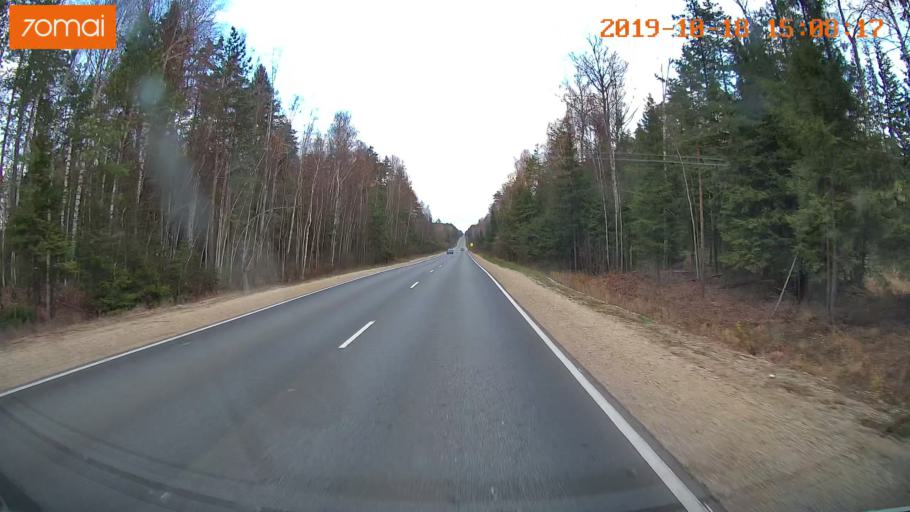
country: RU
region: Vladimir
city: Gus'-Khrustal'nyy
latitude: 55.5502
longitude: 40.6089
